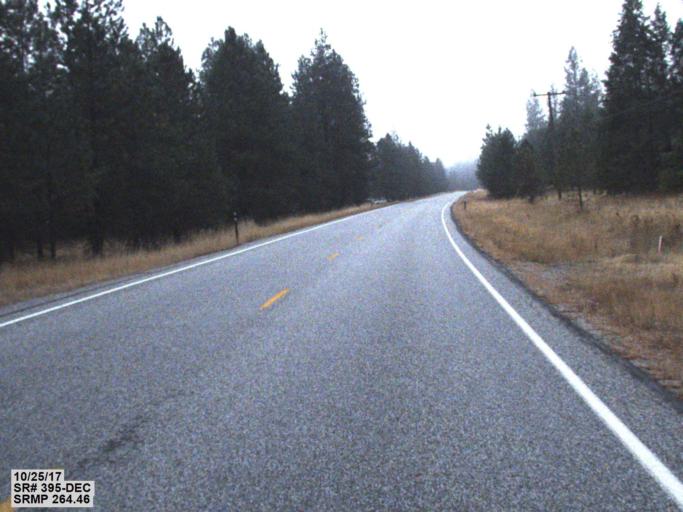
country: CA
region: British Columbia
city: Grand Forks
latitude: 48.9207
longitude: -118.2117
